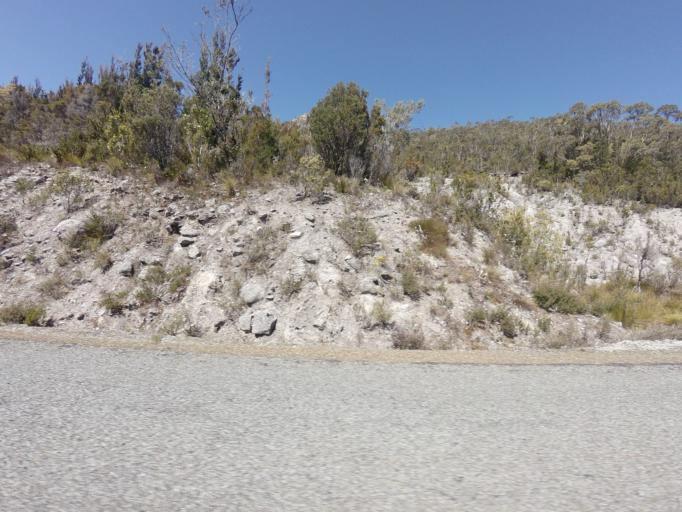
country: AU
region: Tasmania
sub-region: Huon Valley
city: Geeveston
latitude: -42.8039
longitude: 146.3947
